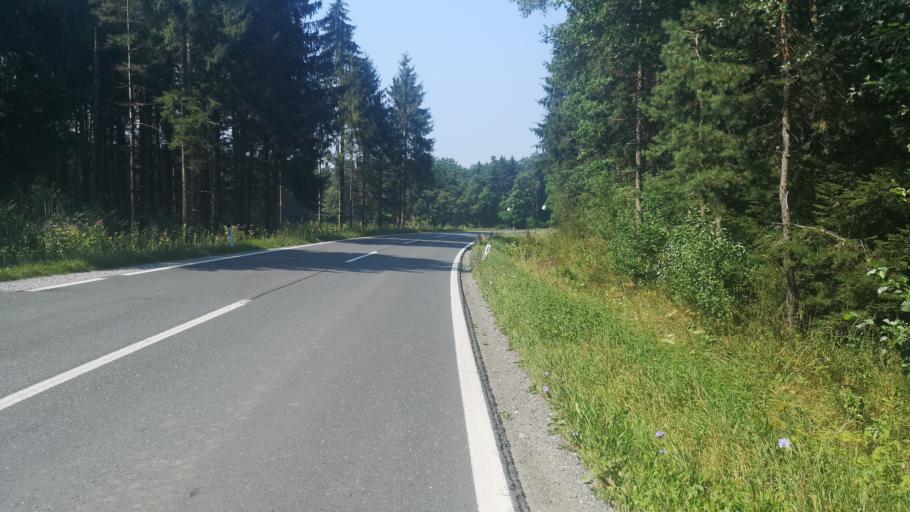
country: AT
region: Styria
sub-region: Politischer Bezirk Graz-Umgebung
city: Unterpremstatten
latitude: 46.9725
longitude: 15.3787
